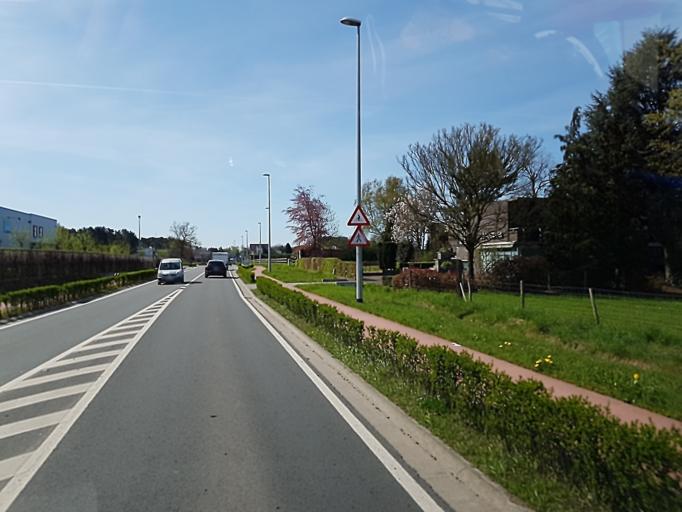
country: BE
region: Flanders
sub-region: Provincie Antwerpen
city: Herselt
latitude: 51.0650
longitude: 4.8918
